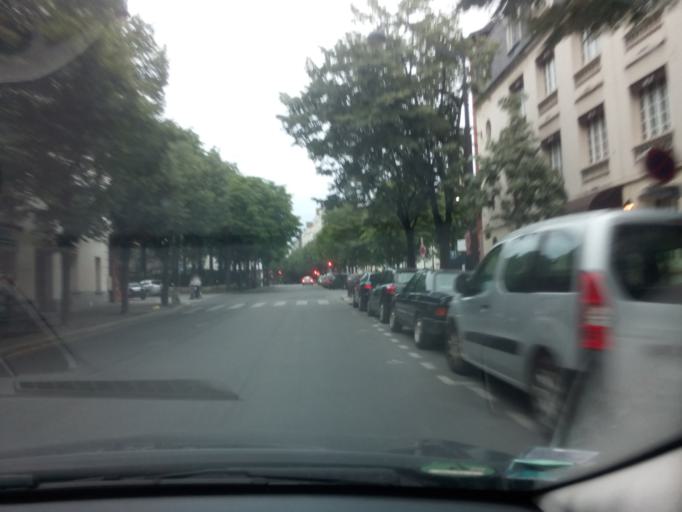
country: FR
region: Ile-de-France
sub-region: Departement du Val-de-Marne
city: Le Kremlin-Bicetre
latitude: 48.8271
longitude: 2.3518
